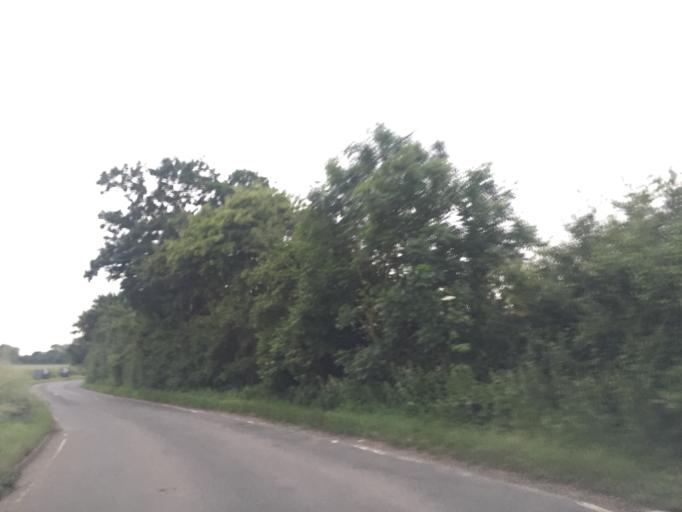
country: GB
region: England
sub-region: Essex
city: Chipping Ongar
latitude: 51.7332
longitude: 0.2274
